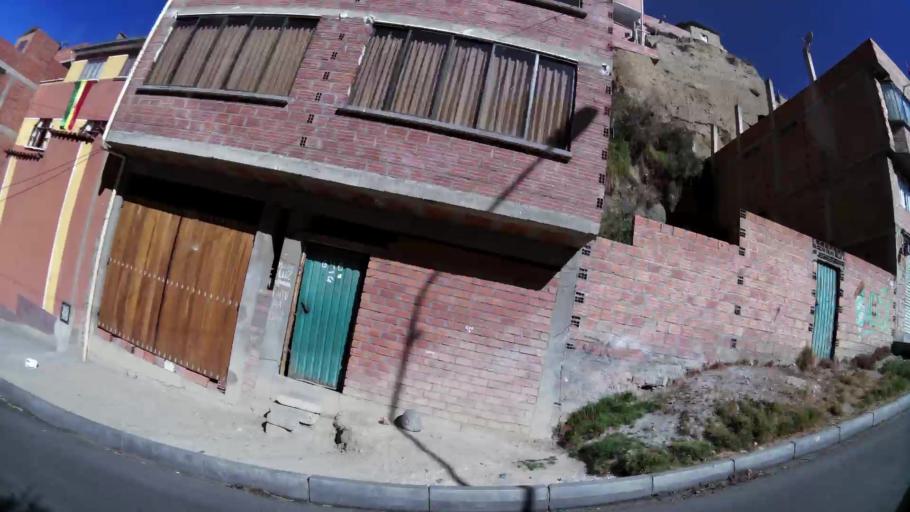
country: BO
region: La Paz
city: La Paz
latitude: -16.5105
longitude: -68.1478
